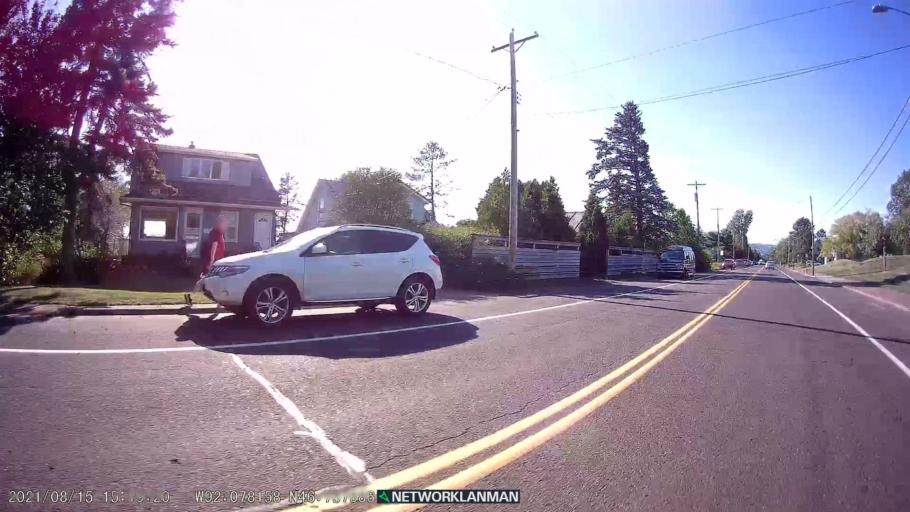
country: US
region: Minnesota
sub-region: Saint Louis County
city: Duluth
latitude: 46.7580
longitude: -92.0784
